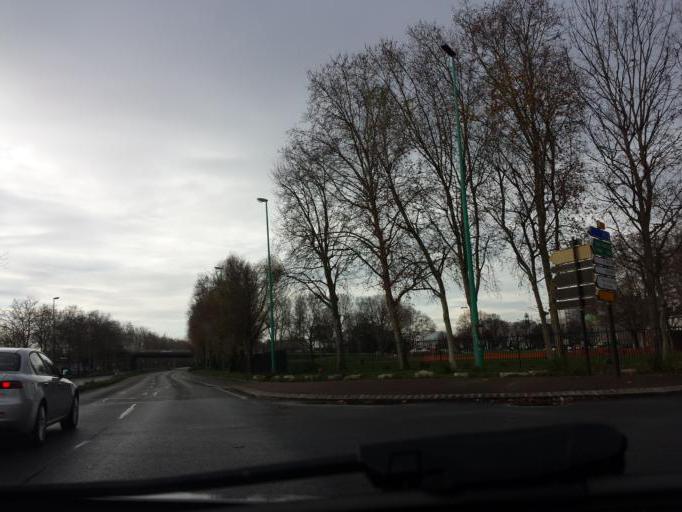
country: FR
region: Ile-de-France
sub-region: Departement du Val-d'Oise
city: Argenteuil
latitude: 48.9427
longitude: 2.2568
